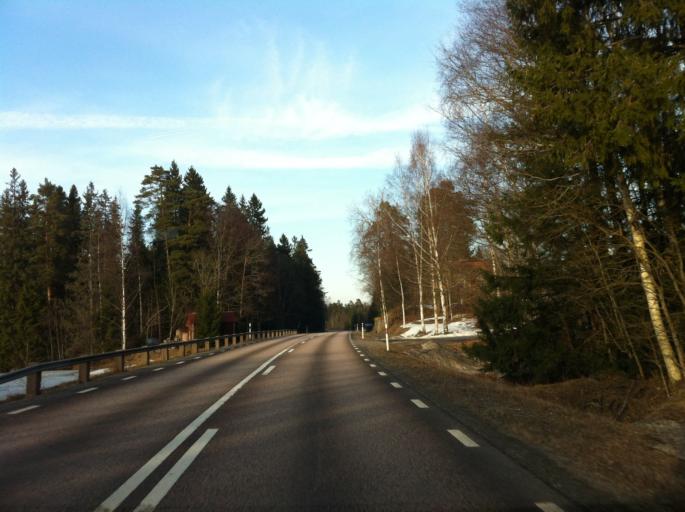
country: SE
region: Vaermland
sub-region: Filipstads Kommun
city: Lesjofors
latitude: 59.8458
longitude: 14.2578
